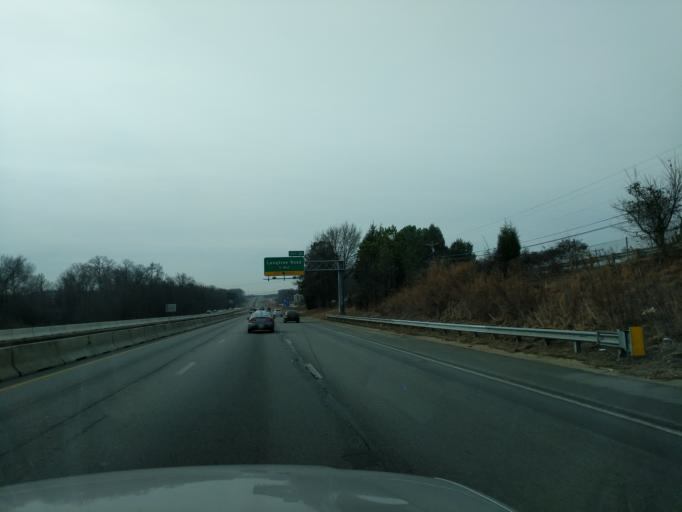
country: US
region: North Carolina
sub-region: Gaston County
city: Davidson
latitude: 35.5481
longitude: -80.8586
